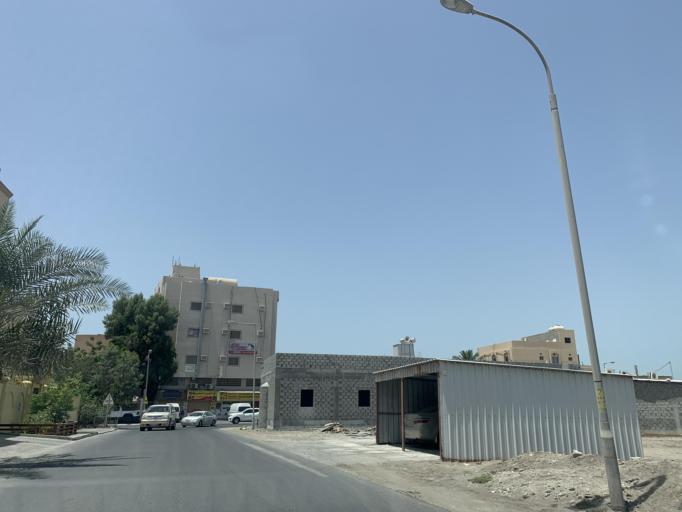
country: BH
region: Northern
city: Sitrah
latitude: 26.1727
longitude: 50.6070
